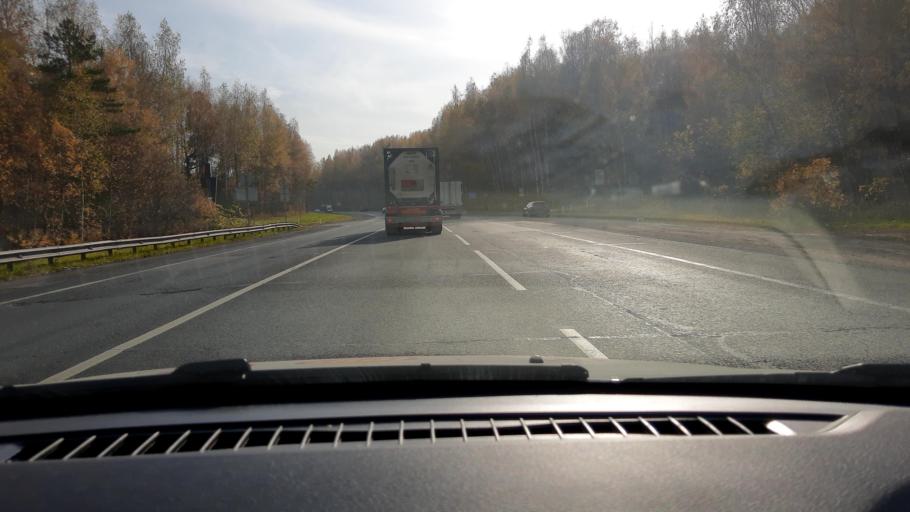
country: RU
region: Nizjnij Novgorod
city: Pamyat' Parizhskoy Kommuny
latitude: 56.0682
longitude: 44.3745
